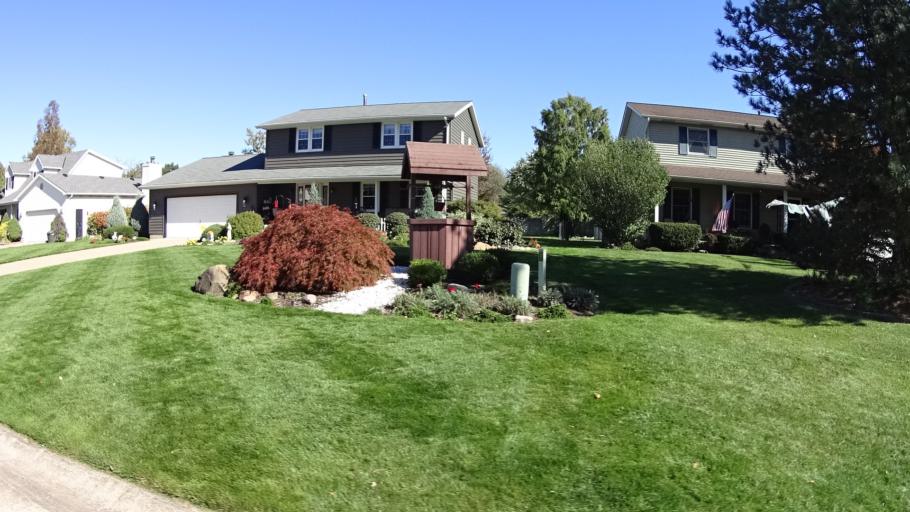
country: US
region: Ohio
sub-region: Lorain County
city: Amherst
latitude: 41.3991
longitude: -82.1934
